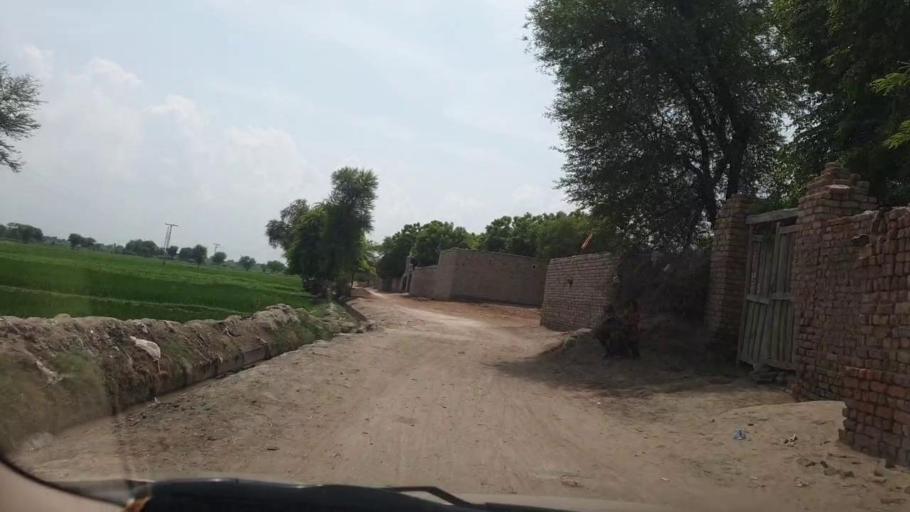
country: PK
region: Sindh
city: Larkana
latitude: 27.5907
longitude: 68.1207
